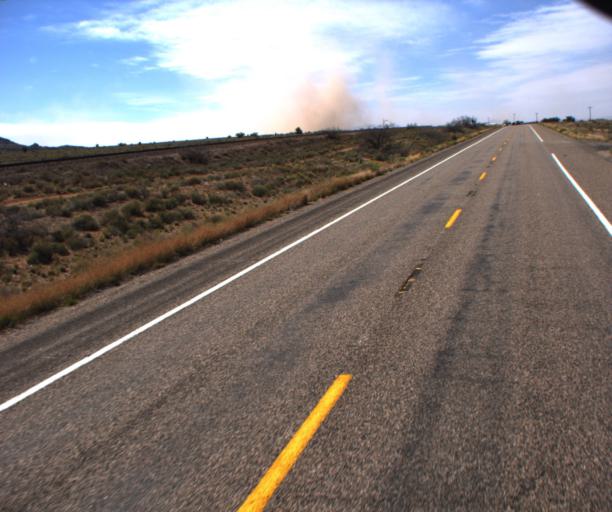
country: US
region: Arizona
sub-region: Mohave County
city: New Kingman-Butler
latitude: 35.4080
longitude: -113.7727
